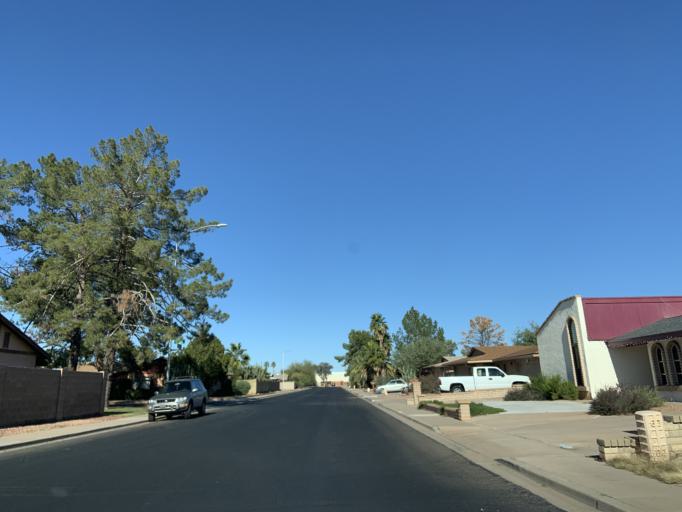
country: US
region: Arizona
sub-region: Maricopa County
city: San Carlos
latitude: 33.3605
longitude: -111.8606
